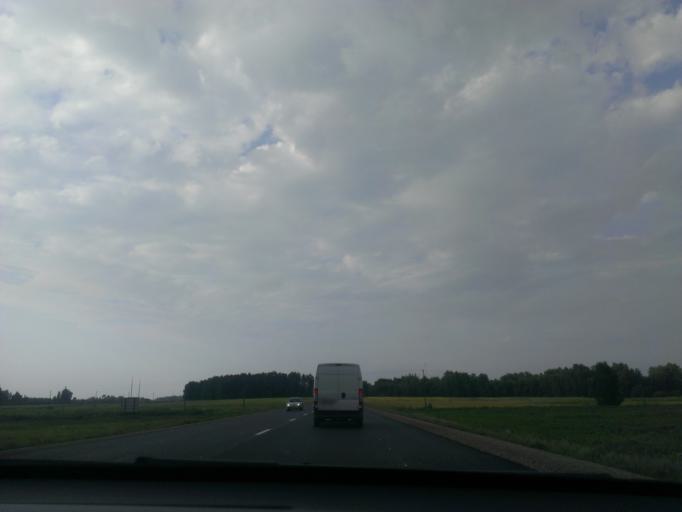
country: LV
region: Lecava
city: Iecava
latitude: 56.6473
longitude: 24.2284
